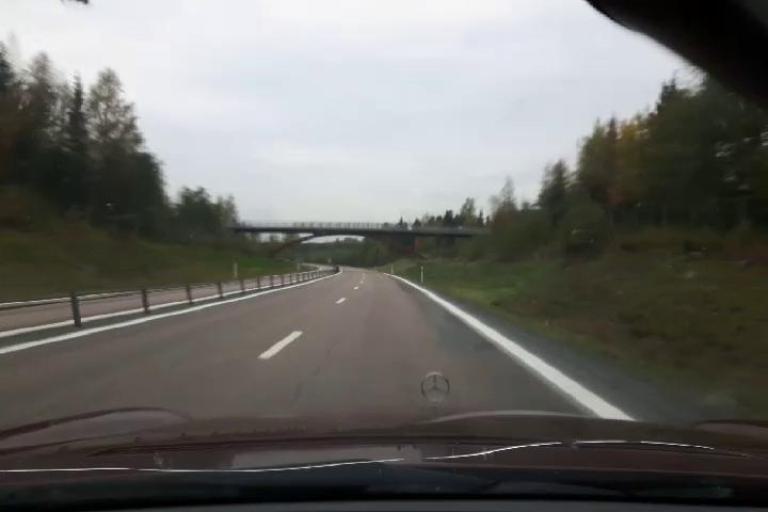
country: SE
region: Vaesternorrland
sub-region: Haernoesands Kommun
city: Haernoesand
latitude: 62.8697
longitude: 18.0409
